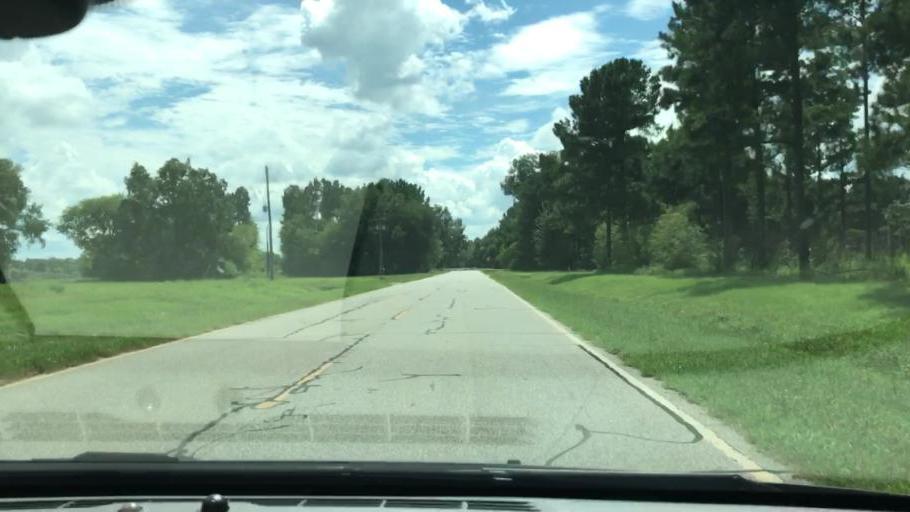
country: US
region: Georgia
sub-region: Quitman County
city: Georgetown
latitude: 32.0509
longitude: -85.0364
